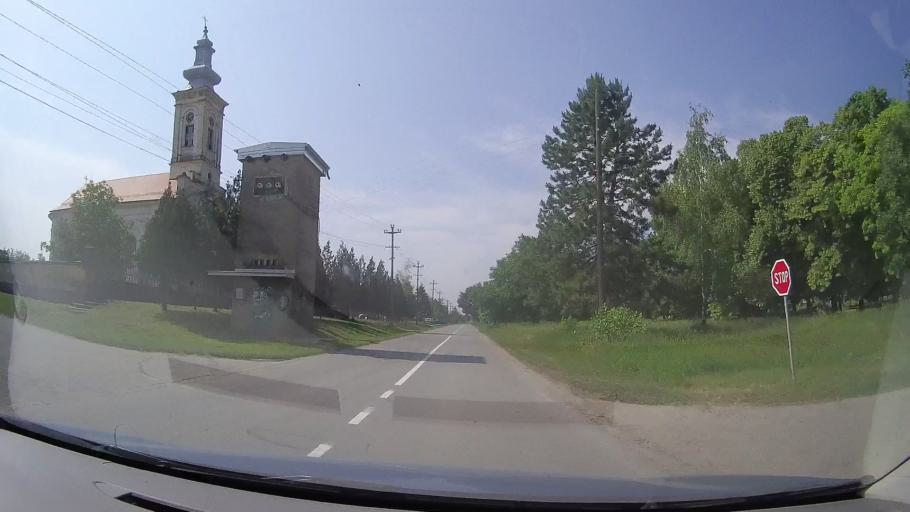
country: RS
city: Samos
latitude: 45.2025
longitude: 20.7728
